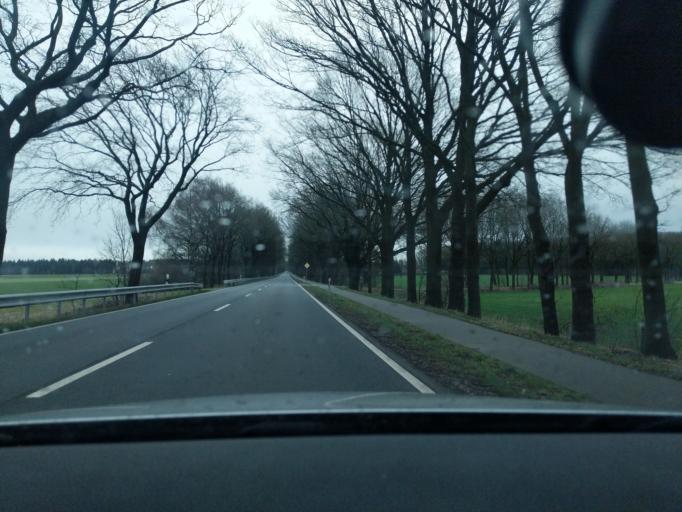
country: DE
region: Lower Saxony
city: Dudenbuttel
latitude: 53.5536
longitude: 9.3552
